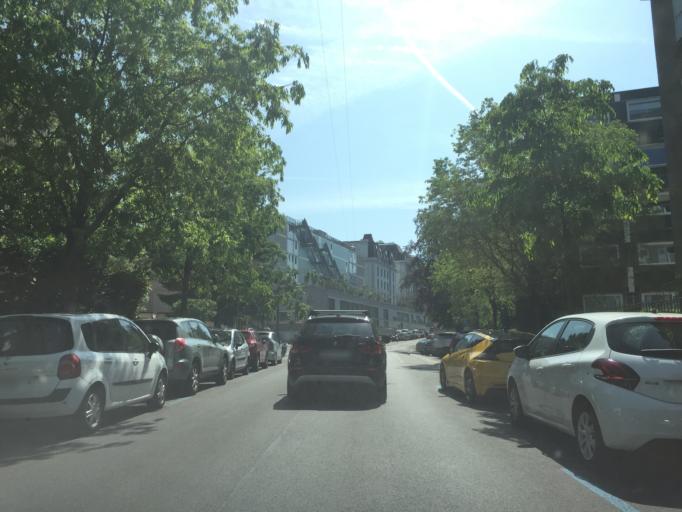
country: CH
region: Vaud
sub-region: Lausanne District
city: Lausanne
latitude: 46.5139
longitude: 6.6300
